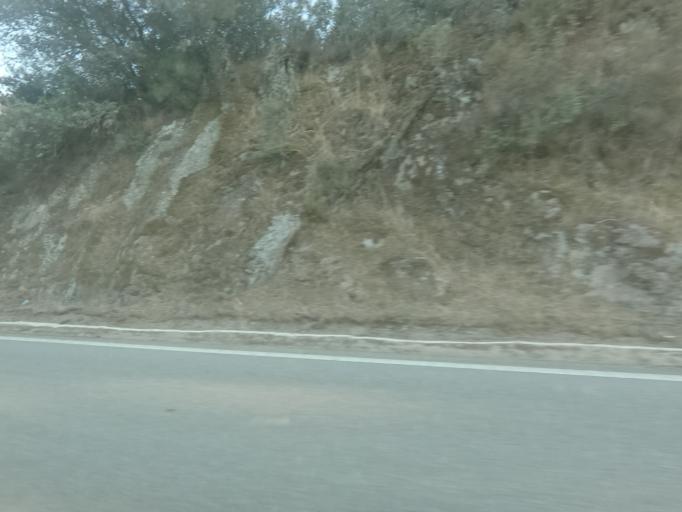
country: PT
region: Viseu
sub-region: Armamar
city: Armamar
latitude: 41.1588
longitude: -7.6465
